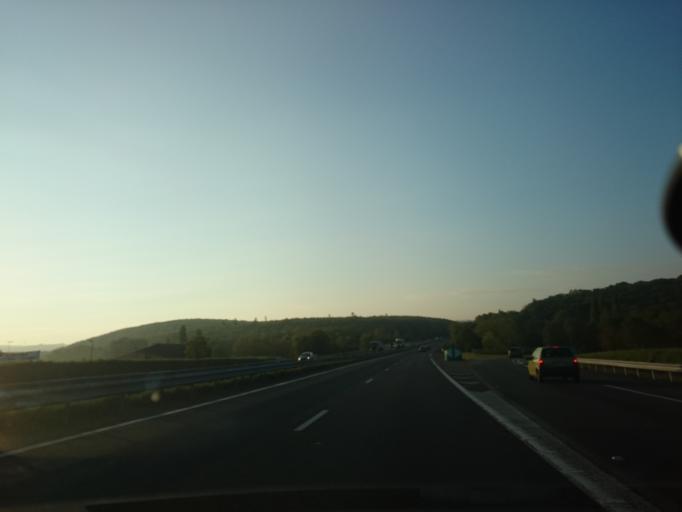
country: FR
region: Brittany
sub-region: Departement du Finistere
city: Le Faou
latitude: 48.2982
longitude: -4.1726
